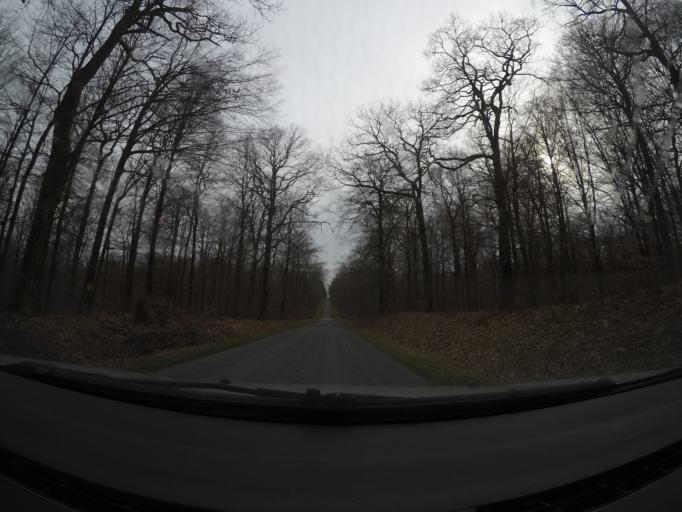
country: BE
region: Wallonia
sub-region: Province du Luxembourg
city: Fauvillers
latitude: 49.7759
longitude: 5.6767
